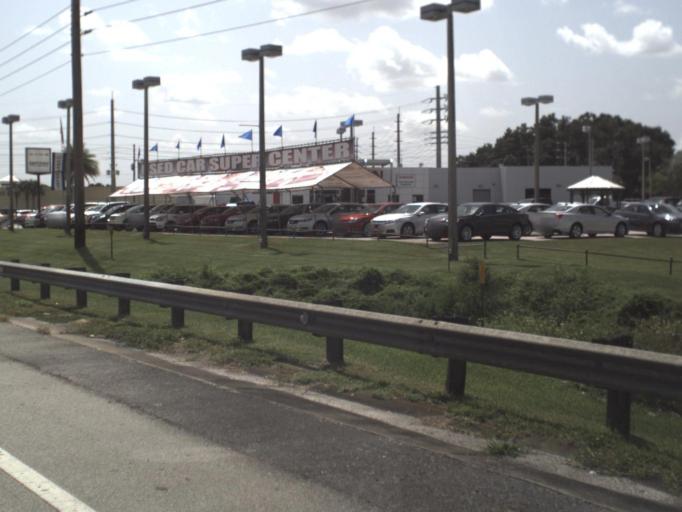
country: US
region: Florida
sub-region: Highlands County
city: Sebring
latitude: 27.4869
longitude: -81.4816
